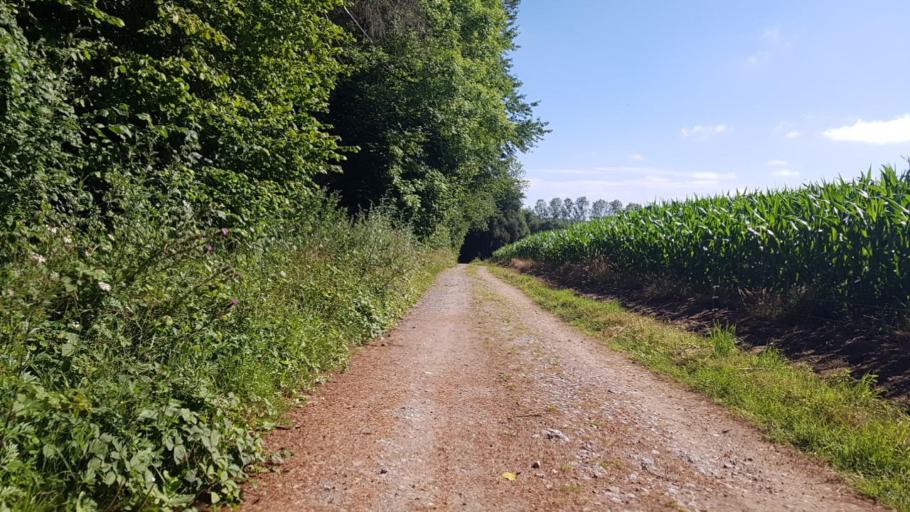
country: FR
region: Nord-Pas-de-Calais
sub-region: Departement du Nord
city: Anor
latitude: 49.9707
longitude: 4.1184
